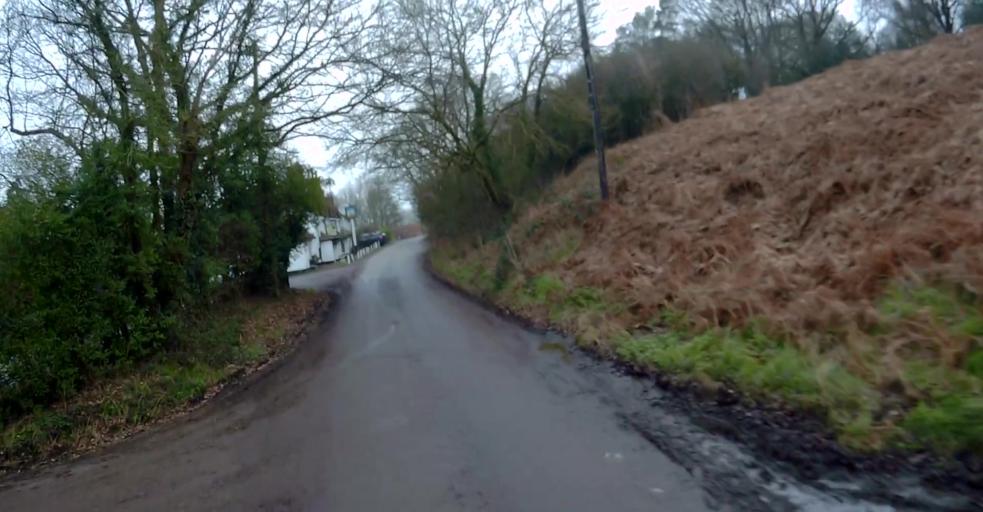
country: GB
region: England
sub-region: Hampshire
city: Hook
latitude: 51.3255
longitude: -0.9348
